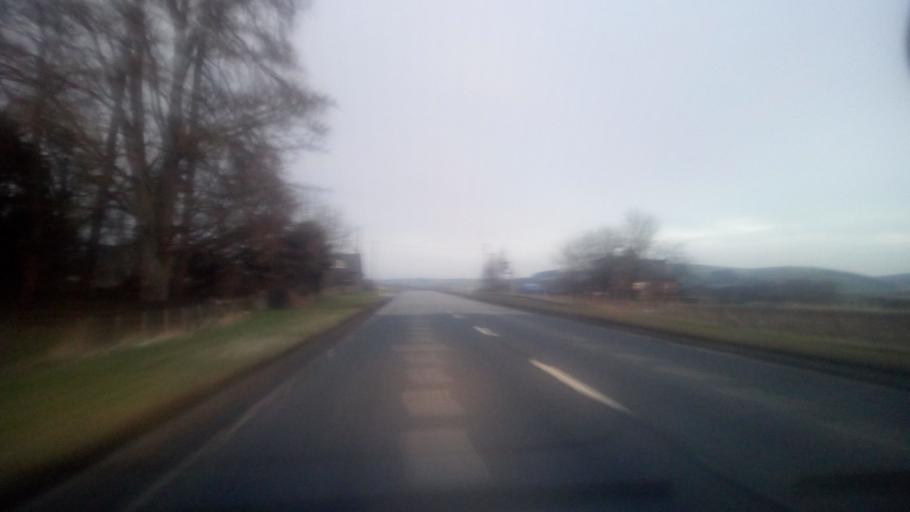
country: GB
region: Scotland
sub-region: The Scottish Borders
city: Lauder
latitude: 55.7486
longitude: -2.7721
